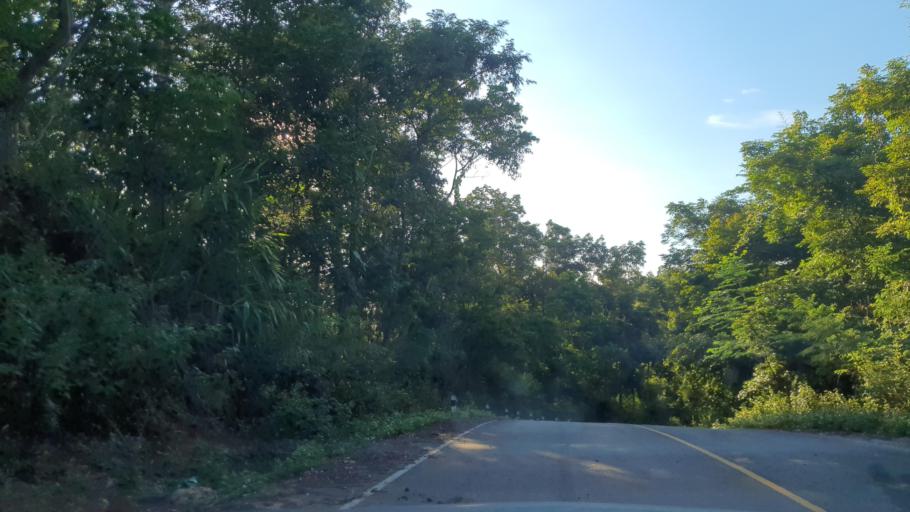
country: TH
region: Chiang Mai
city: Mae On
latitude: 18.8066
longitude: 99.3045
